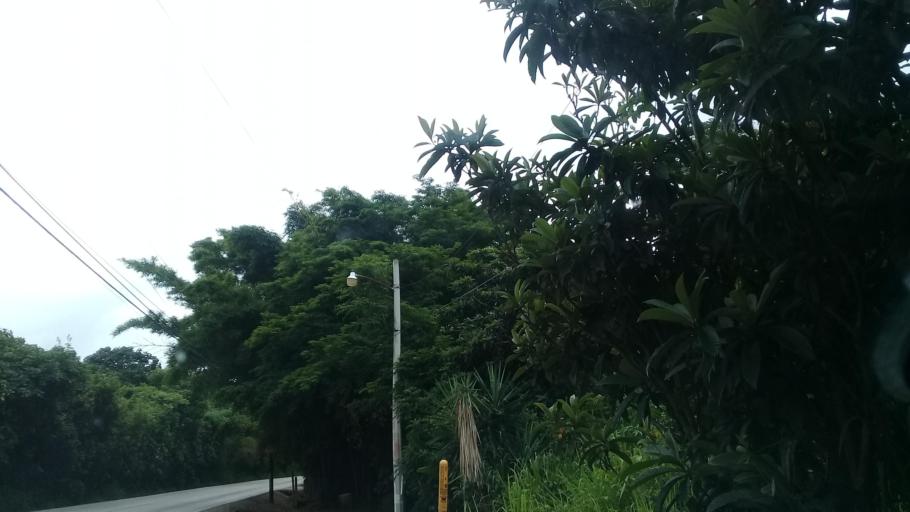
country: MX
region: Veracruz
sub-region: Emiliano Zapata
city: Jacarandas
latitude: 19.4787
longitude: -96.8574
